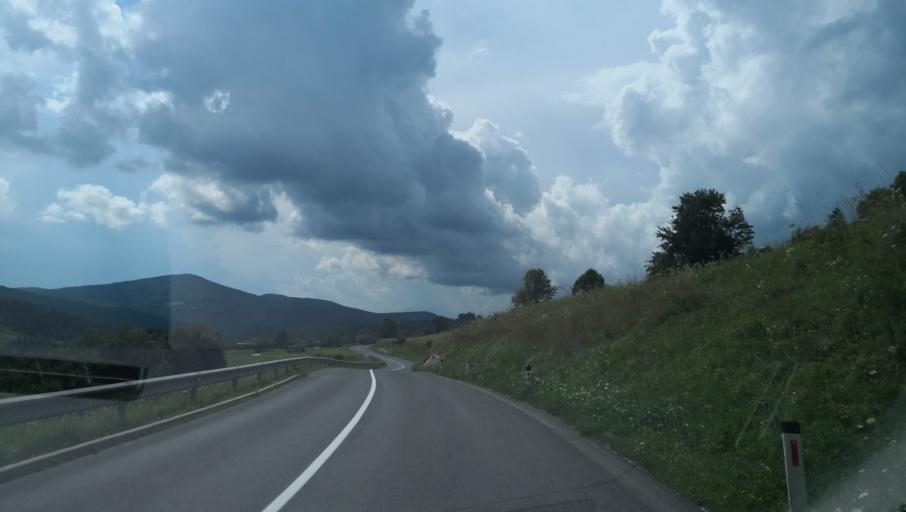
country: SI
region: Zuzemberk
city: Zuzemberk
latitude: 45.8575
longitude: 14.8677
